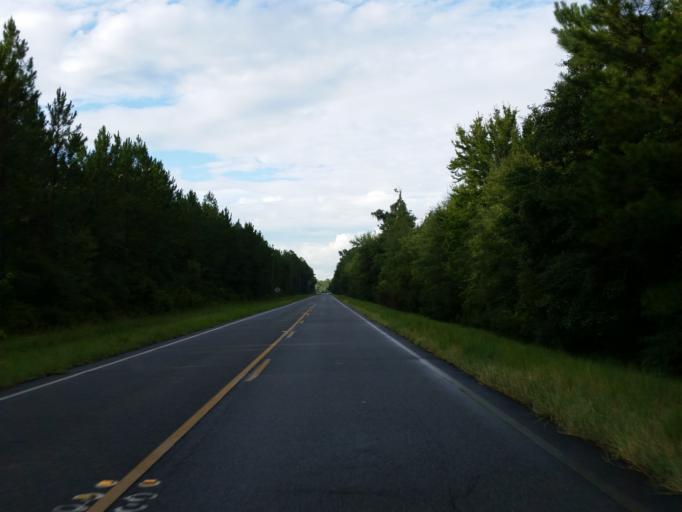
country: US
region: Florida
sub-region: Hamilton County
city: Jasper
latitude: 30.6604
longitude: -82.5595
